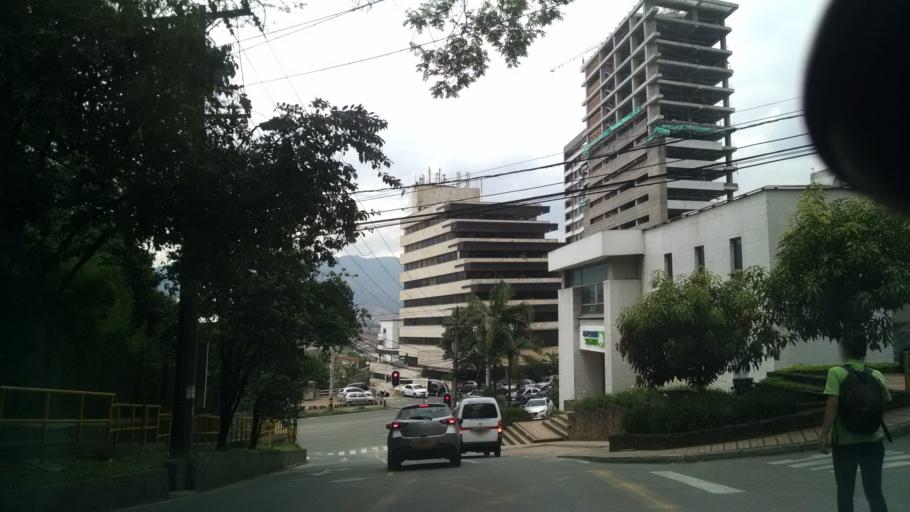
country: CO
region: Antioquia
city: Medellin
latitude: 6.2146
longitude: -75.5694
